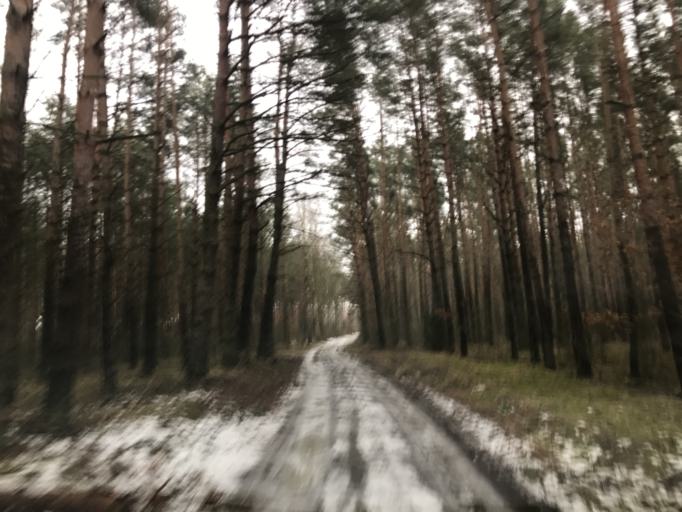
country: PL
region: Kujawsko-Pomorskie
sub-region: Powiat brodnicki
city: Bartniczka
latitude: 53.2841
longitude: 19.5769
